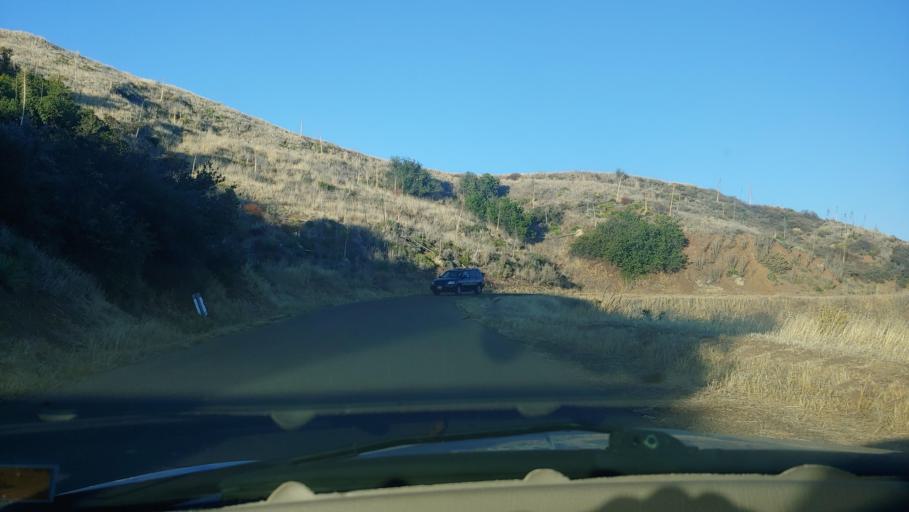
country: US
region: California
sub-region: Santa Barbara County
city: Goleta
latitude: 34.5187
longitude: -119.7854
